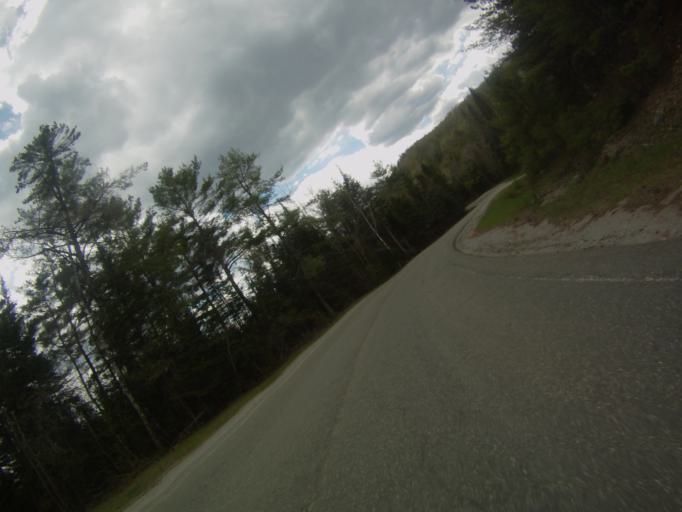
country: US
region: New York
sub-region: Essex County
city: Mineville
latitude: 44.0879
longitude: -73.5851
